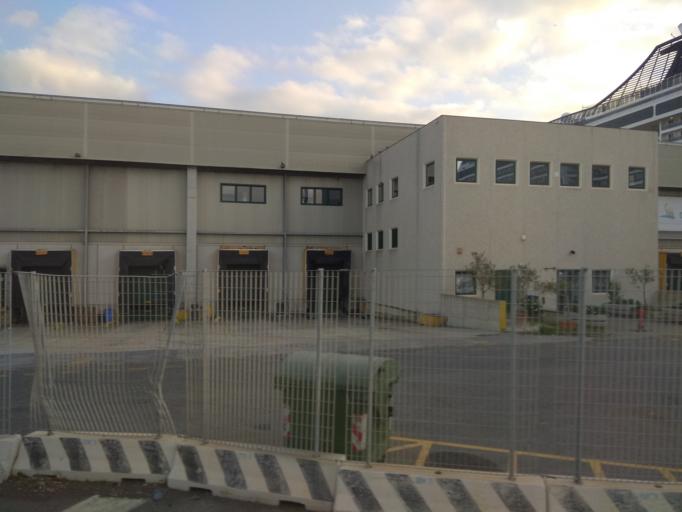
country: IT
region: Latium
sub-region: Citta metropolitana di Roma Capitale
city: Civitavecchia
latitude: 42.1031
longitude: 11.7750
